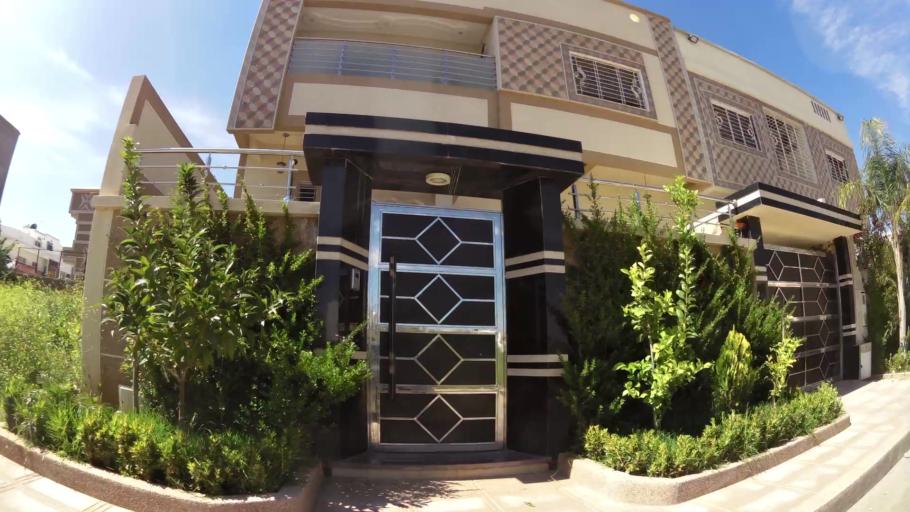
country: MA
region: Fes-Boulemane
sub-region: Fes
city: Fes
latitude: 34.0021
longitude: -4.9880
